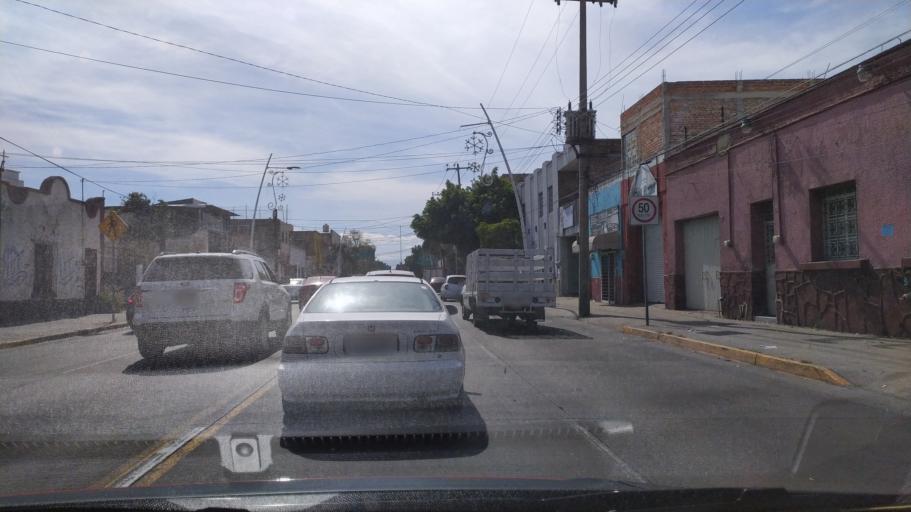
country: MX
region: Jalisco
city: Tlaquepaque
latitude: 20.6666
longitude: -103.3325
